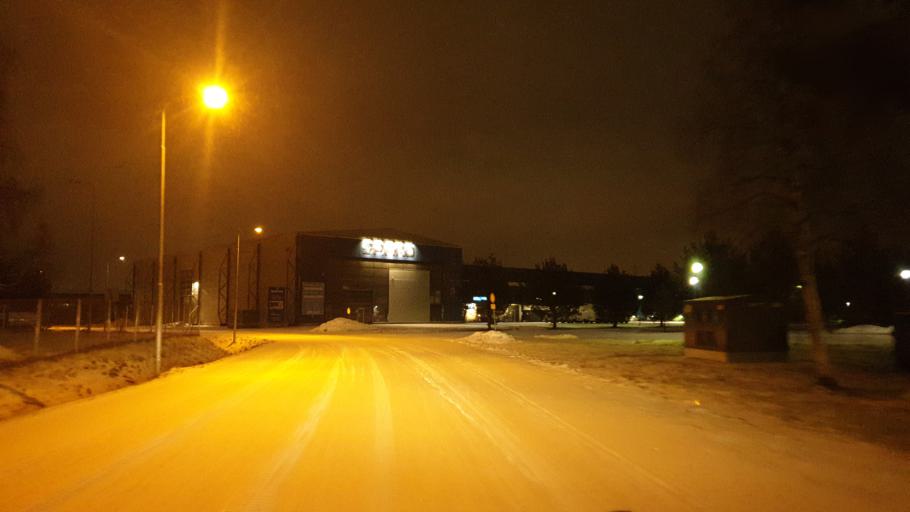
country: FI
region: Northern Ostrobothnia
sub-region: Oulu
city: Oulu
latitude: 64.9935
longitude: 25.4506
